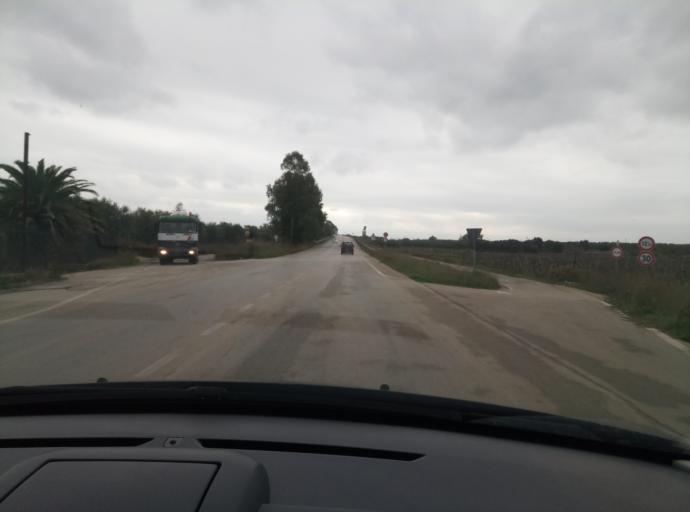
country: IT
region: Apulia
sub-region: Provincia di Bari
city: Acquaviva delle Fonti
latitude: 40.9258
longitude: 16.8589
